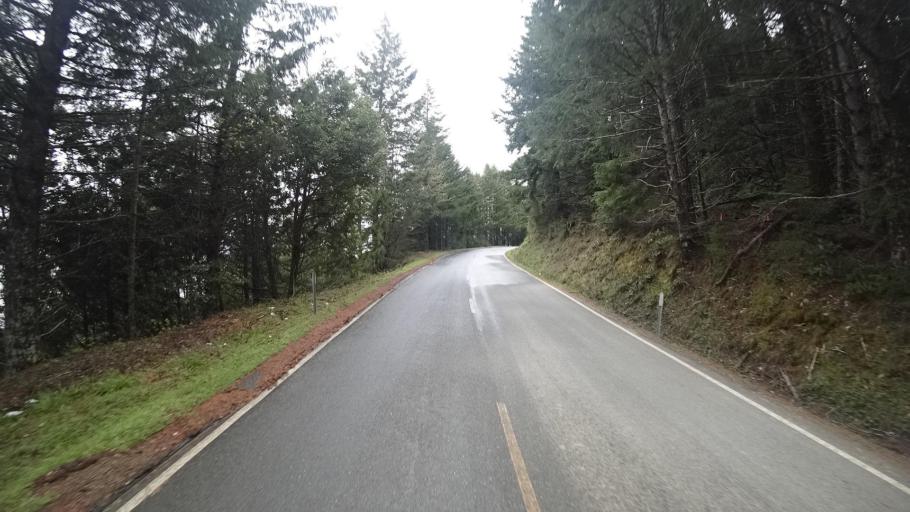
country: US
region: California
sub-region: Humboldt County
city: Westhaven-Moonstone
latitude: 41.1409
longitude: -123.8577
